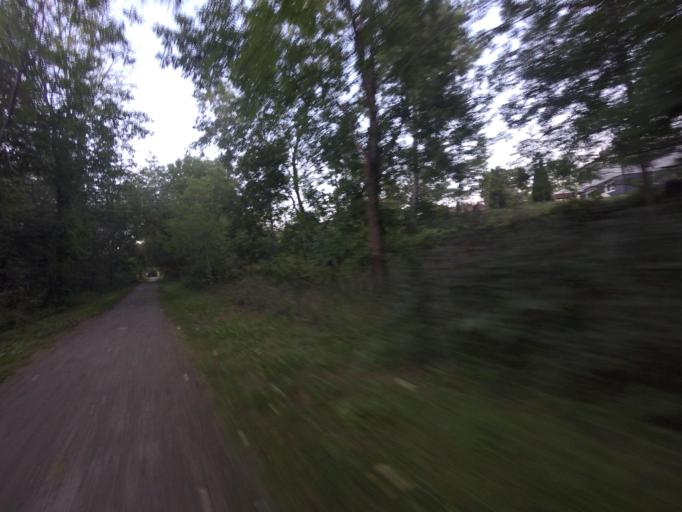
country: CA
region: Ontario
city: Orangeville
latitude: 43.9509
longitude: -79.8348
